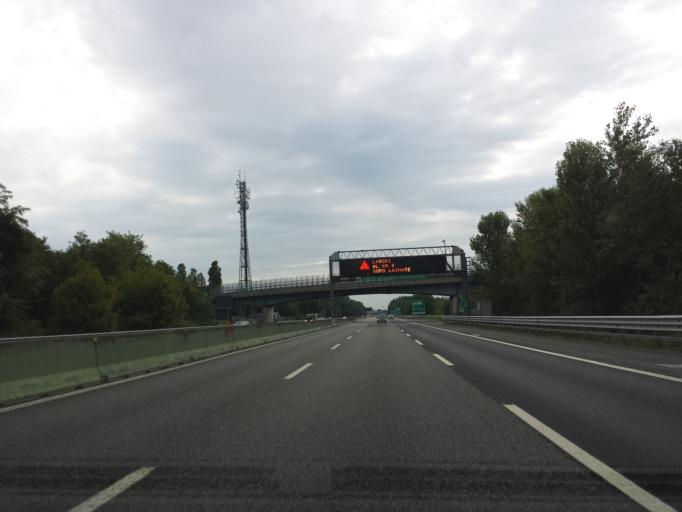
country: IT
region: Lombardy
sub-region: Citta metropolitana di Milano
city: Cantalupo
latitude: 45.5838
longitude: 8.9909
